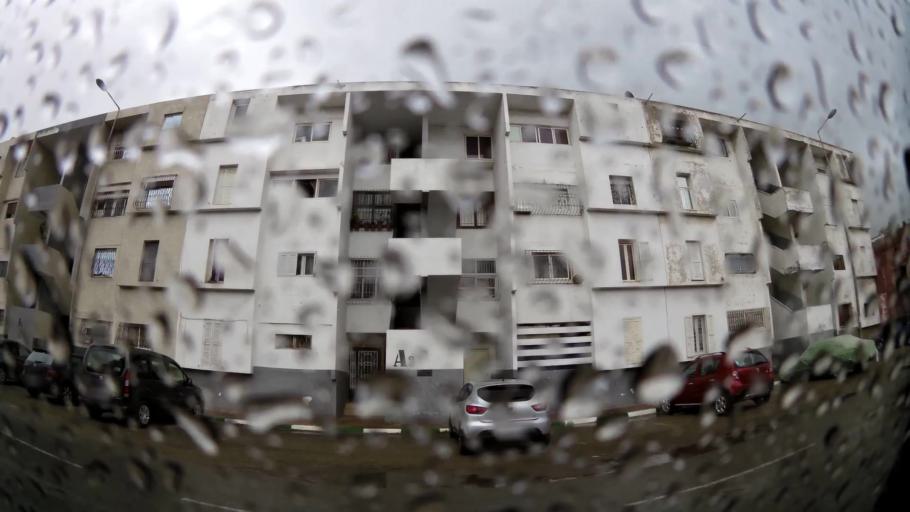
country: MA
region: Grand Casablanca
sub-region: Mediouna
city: Tit Mellil
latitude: 33.6205
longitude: -7.4792
